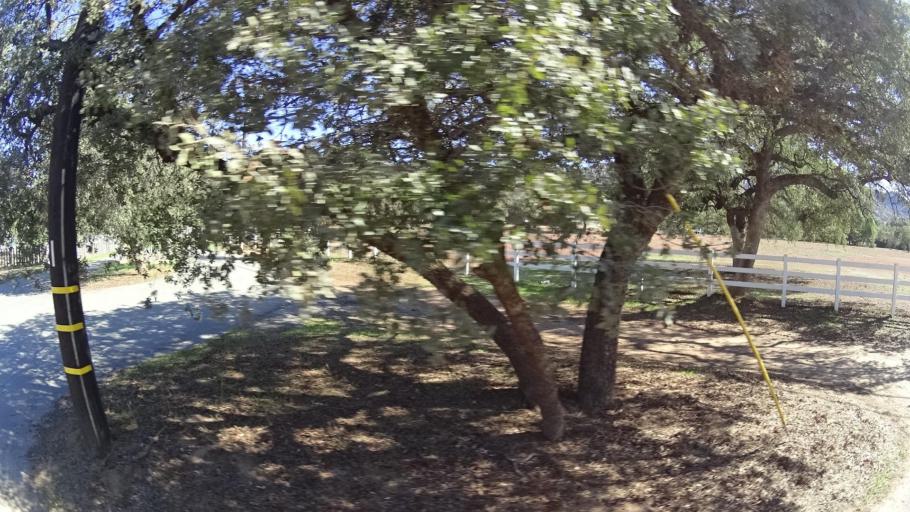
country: US
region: California
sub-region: San Diego County
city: Jamul
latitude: 32.7232
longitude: -116.8122
